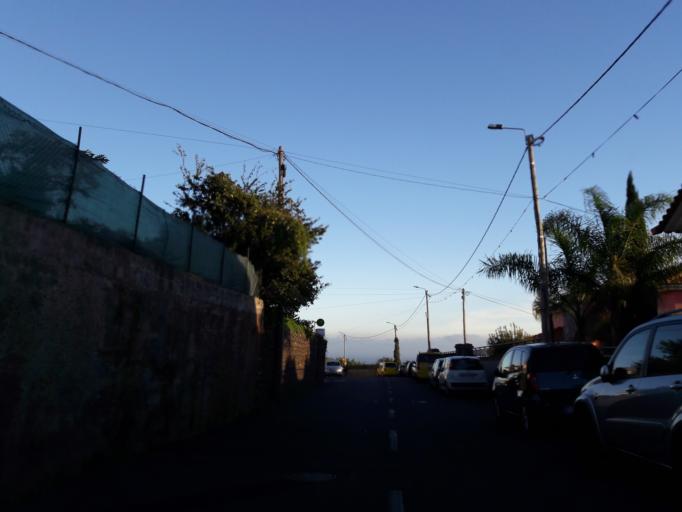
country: PT
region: Madeira
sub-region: Funchal
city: Nossa Senhora do Monte
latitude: 32.6648
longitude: -16.9058
